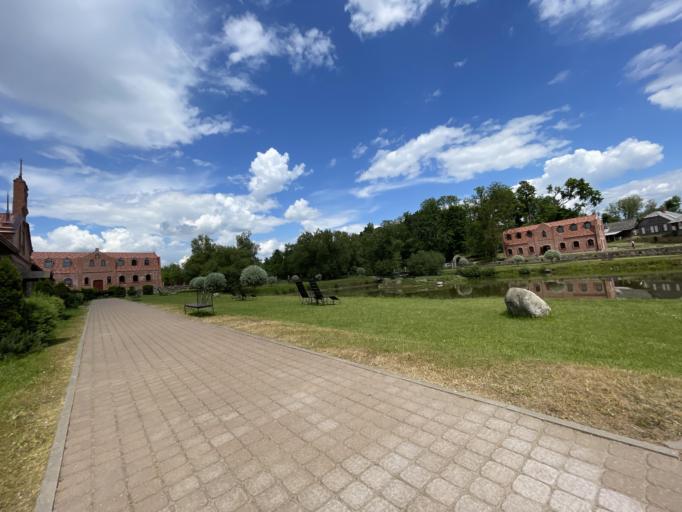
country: BY
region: Minsk
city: Ivyanyets
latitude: 53.7417
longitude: 26.8752
